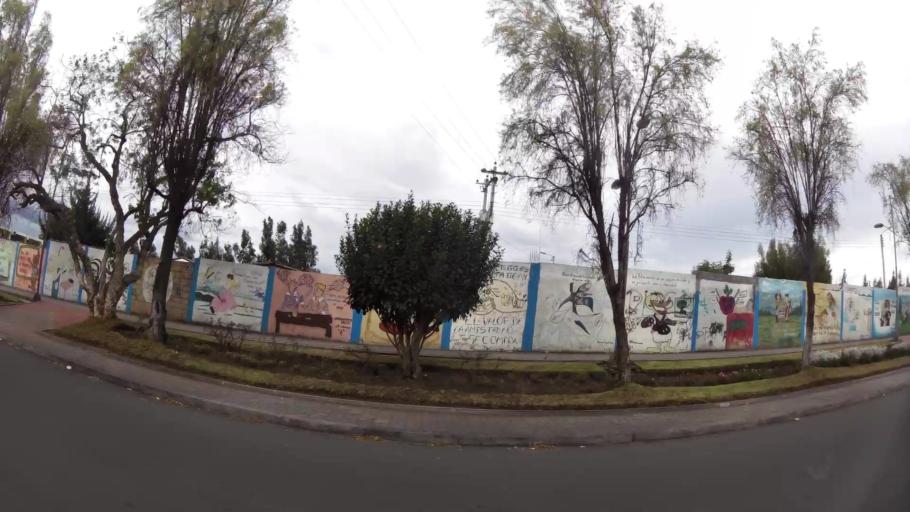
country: EC
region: Tungurahua
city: Ambato
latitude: -1.2543
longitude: -78.6290
